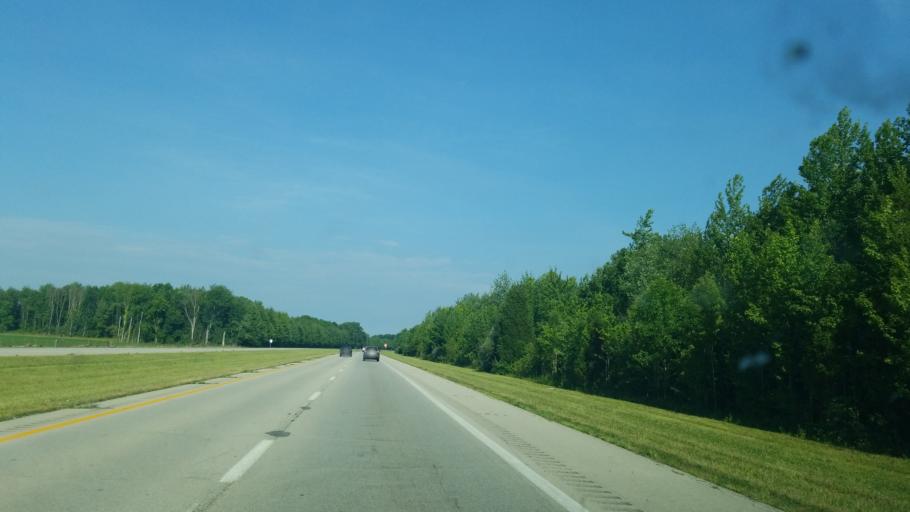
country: US
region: Ohio
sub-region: Clermont County
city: Williamsburg
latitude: 39.0602
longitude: -84.0048
